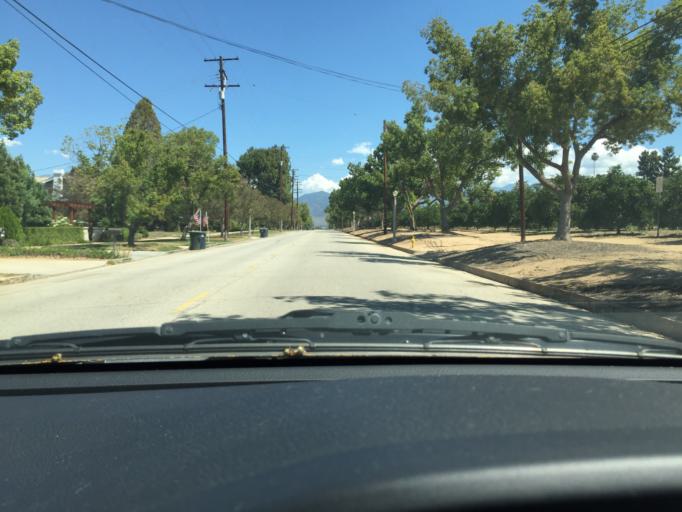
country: US
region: California
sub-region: San Bernardino County
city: Redlands
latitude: 34.0400
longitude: -117.1742
